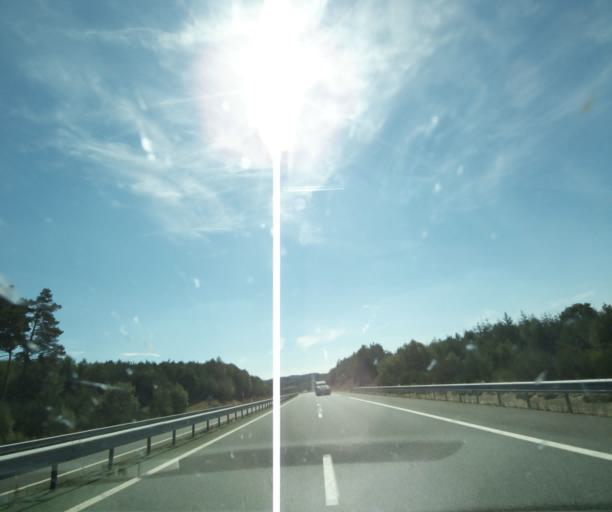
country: FR
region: Limousin
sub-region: Departement de la Correze
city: Ussel
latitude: 45.5660
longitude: 2.3737
